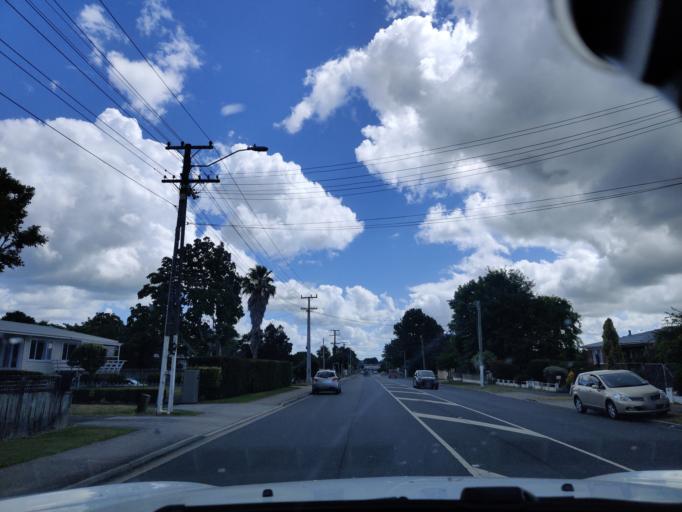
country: NZ
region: Auckland
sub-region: Auckland
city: Papakura
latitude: -37.0588
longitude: 174.9533
